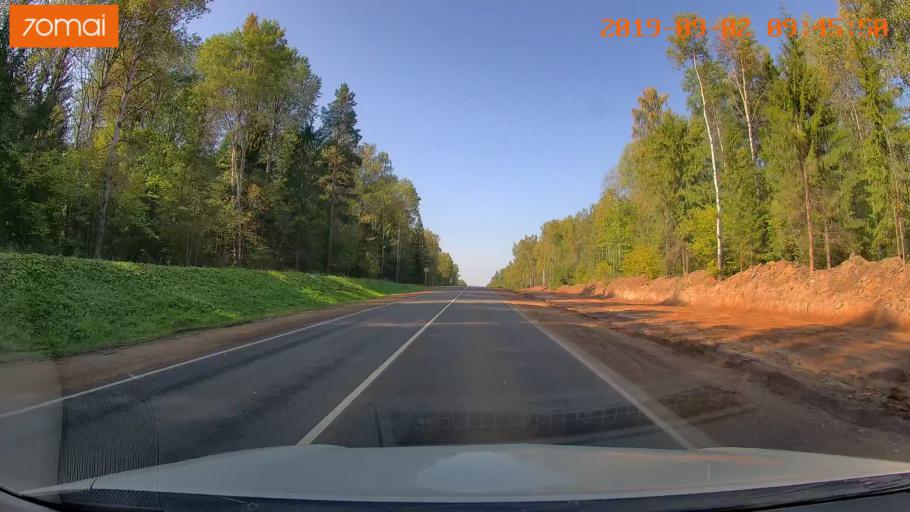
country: RU
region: Kaluga
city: Mosal'sk
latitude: 54.6336
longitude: 34.8421
